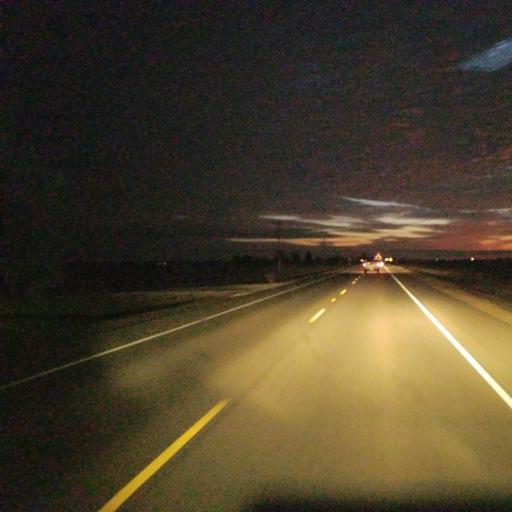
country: US
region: Illinois
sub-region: Peoria County
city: Hanna City
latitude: 40.6975
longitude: -89.8782
